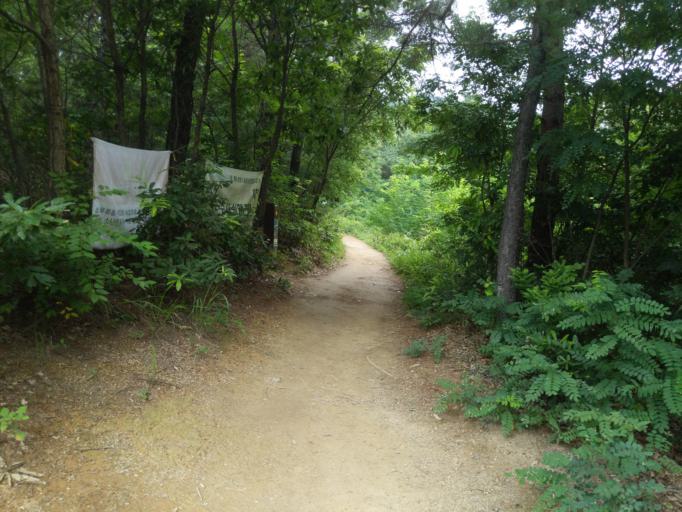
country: KR
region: Daegu
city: Hwawon
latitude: 35.7927
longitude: 128.5236
